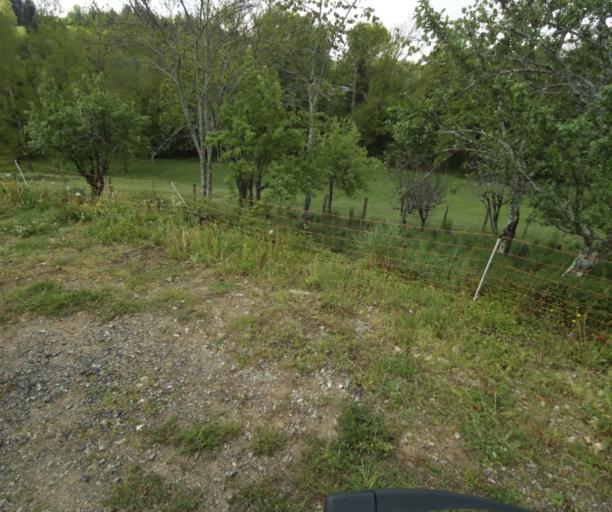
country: FR
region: Limousin
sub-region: Departement de la Correze
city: Tulle
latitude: 45.2794
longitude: 1.7601
